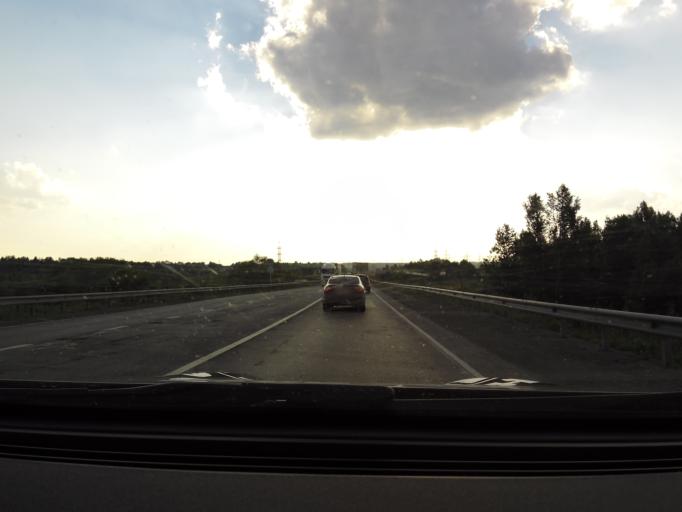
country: RU
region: Sverdlovsk
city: Revda
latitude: 56.8264
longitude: 59.9712
